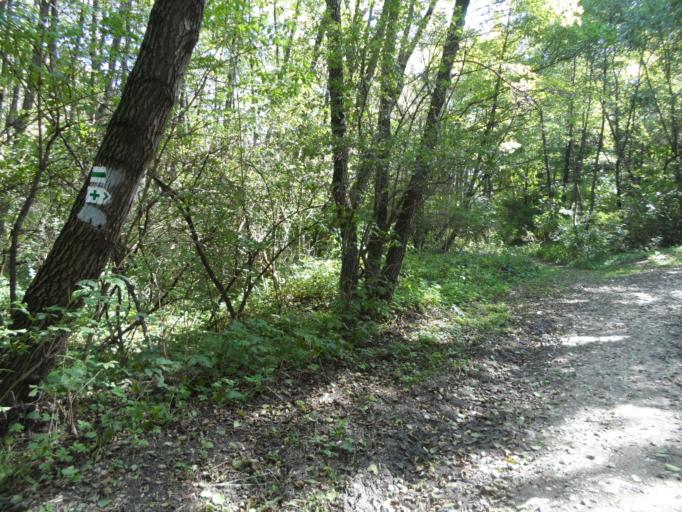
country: HU
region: Veszprem
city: Ajka
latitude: 47.2235
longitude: 17.5542
